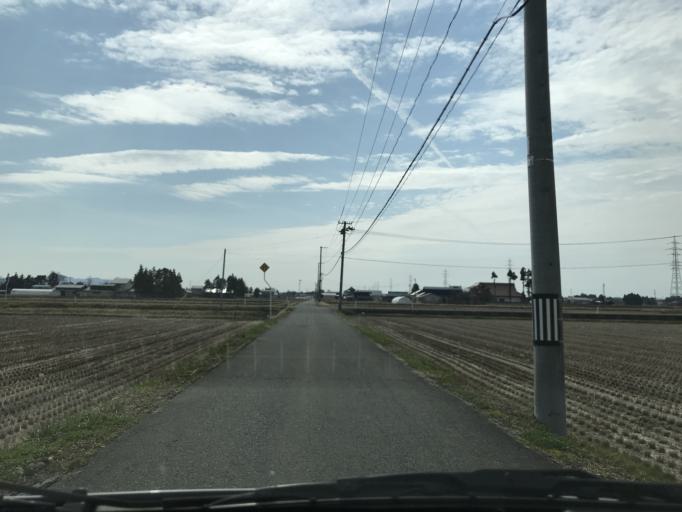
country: JP
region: Iwate
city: Mizusawa
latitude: 39.1506
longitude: 141.0854
